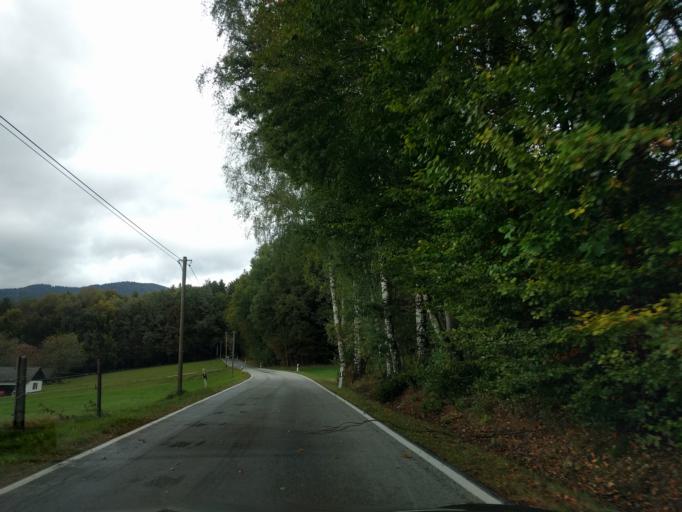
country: DE
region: Bavaria
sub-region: Lower Bavaria
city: Schaufling
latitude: 48.8407
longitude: 13.0902
